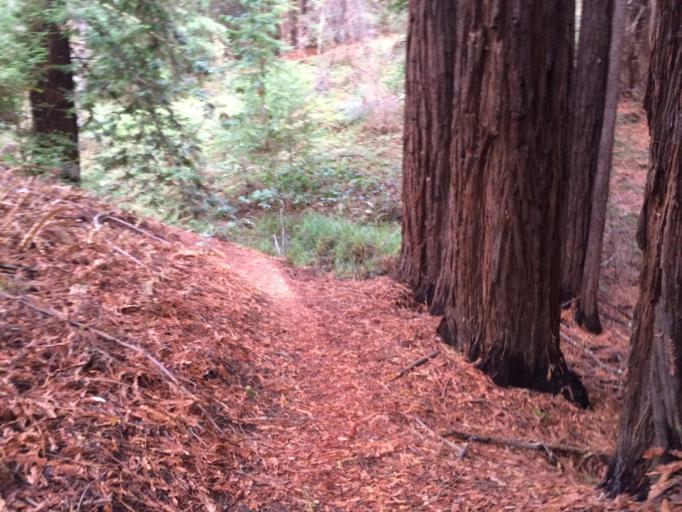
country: US
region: California
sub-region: Santa Cruz County
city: Pasatiempo
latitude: 37.0027
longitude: -122.0579
